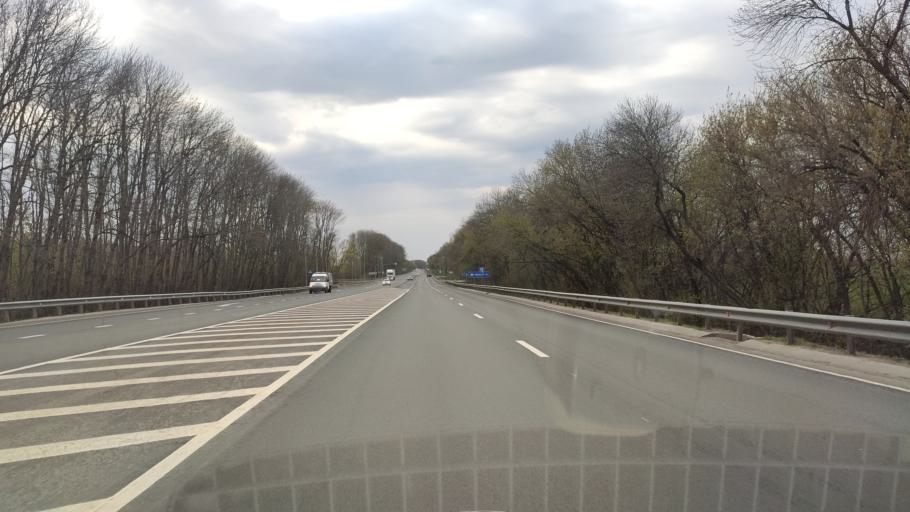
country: RU
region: Voronezj
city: Latnaya
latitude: 51.6474
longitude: 38.7927
